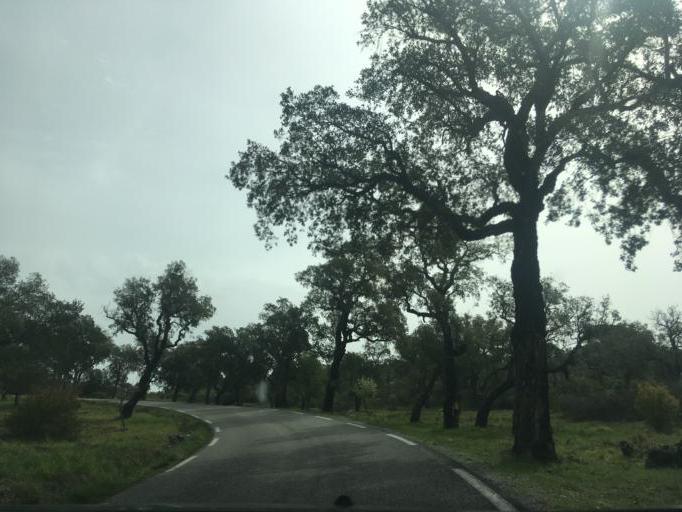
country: FR
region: Provence-Alpes-Cote d'Azur
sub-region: Departement du Var
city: Le Muy
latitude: 43.5141
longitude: 6.6266
